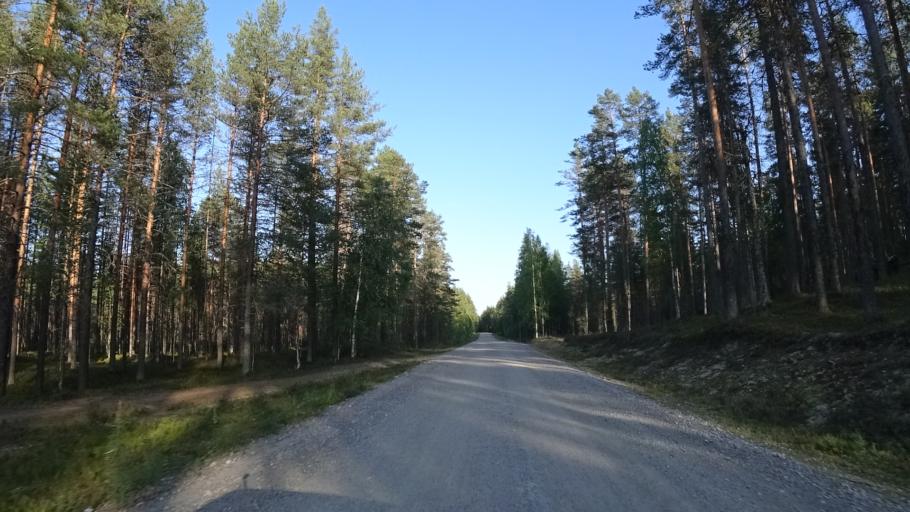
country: FI
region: North Karelia
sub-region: Joensuu
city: Ilomantsi
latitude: 63.1400
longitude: 30.6908
